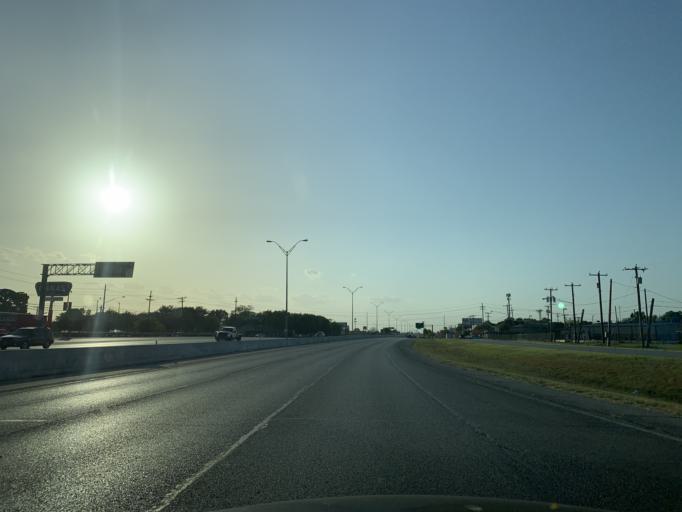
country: US
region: Texas
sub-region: Dallas County
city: Balch Springs
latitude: 32.7094
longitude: -96.6774
